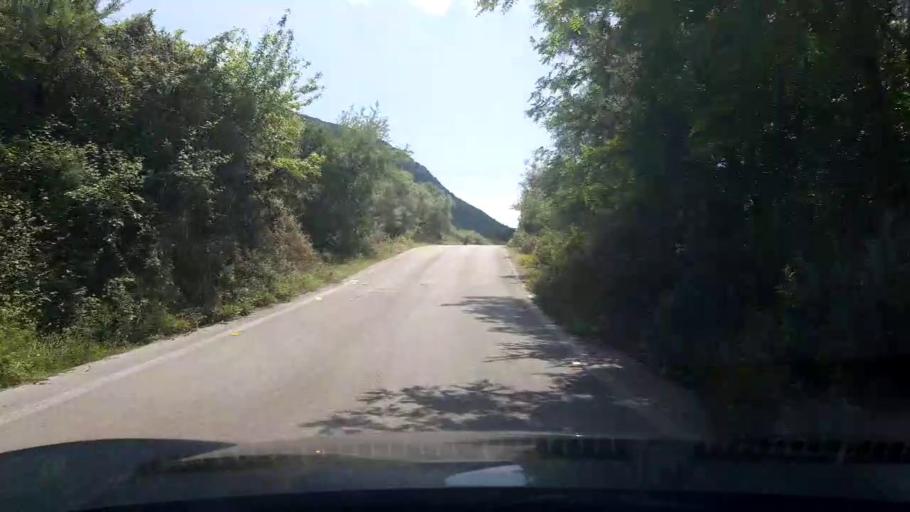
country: GR
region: Ionian Islands
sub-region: Lefkada
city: Nidri
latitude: 38.6488
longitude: 20.7080
